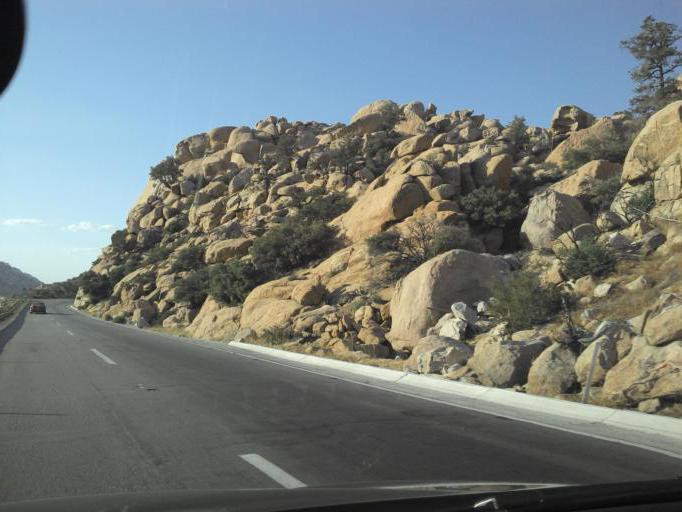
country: MX
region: Baja California
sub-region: Tecate
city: Cereso del Hongo
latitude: 32.5671
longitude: -116.0407
